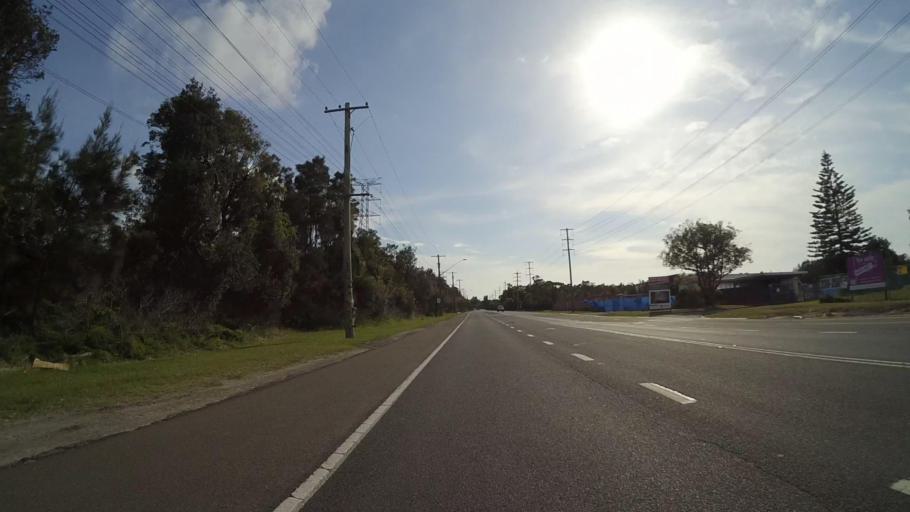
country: AU
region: New South Wales
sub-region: Sutherland Shire
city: Kurnell
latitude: -34.0214
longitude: 151.1986
